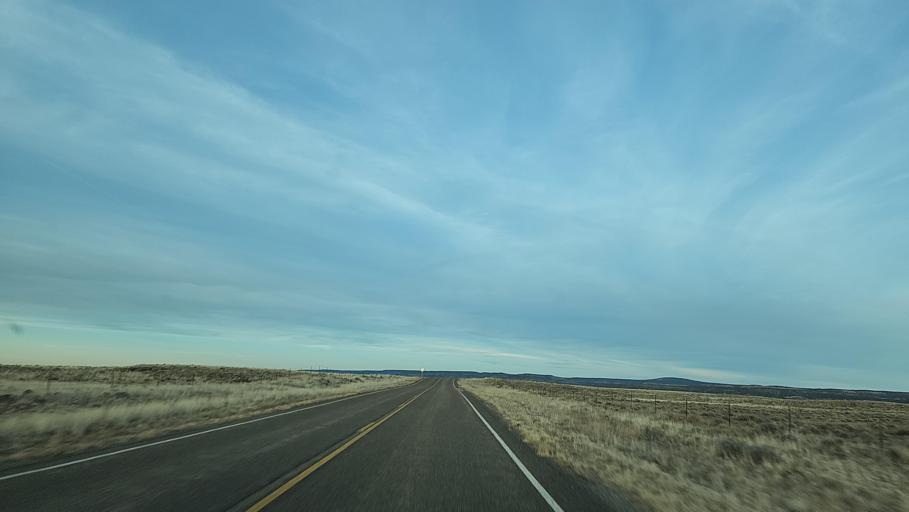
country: US
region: New Mexico
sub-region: Cibola County
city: Grants
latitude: 34.6871
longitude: -108.0641
